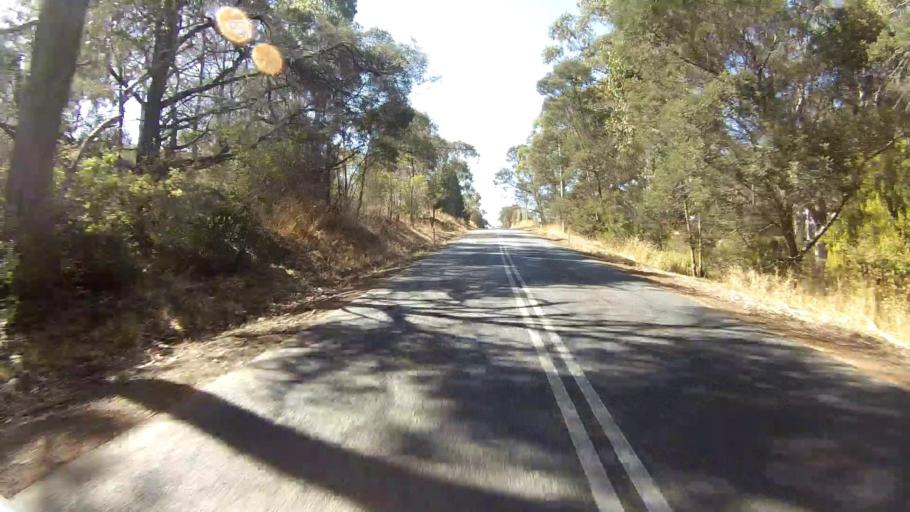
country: AU
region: Tasmania
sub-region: Sorell
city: Sorell
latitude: -42.2606
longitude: 148.0026
